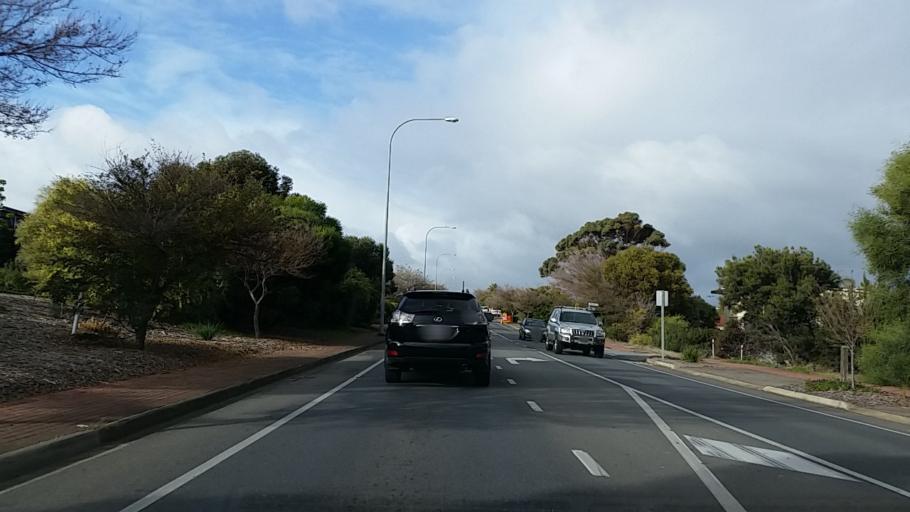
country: AU
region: South Australia
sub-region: Adelaide
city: Port Noarlunga
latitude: -35.1463
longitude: 138.4811
